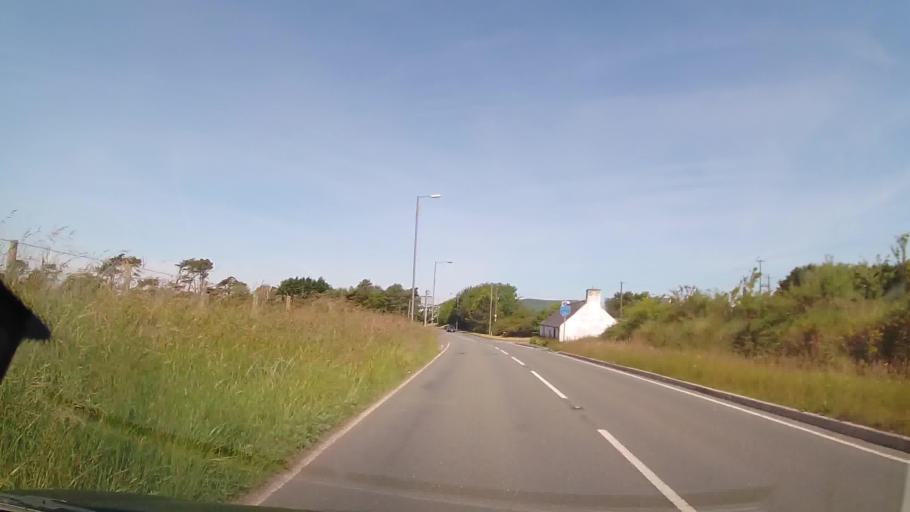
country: GB
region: Wales
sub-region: Gwynedd
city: Tywyn
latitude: 52.5806
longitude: -4.0763
